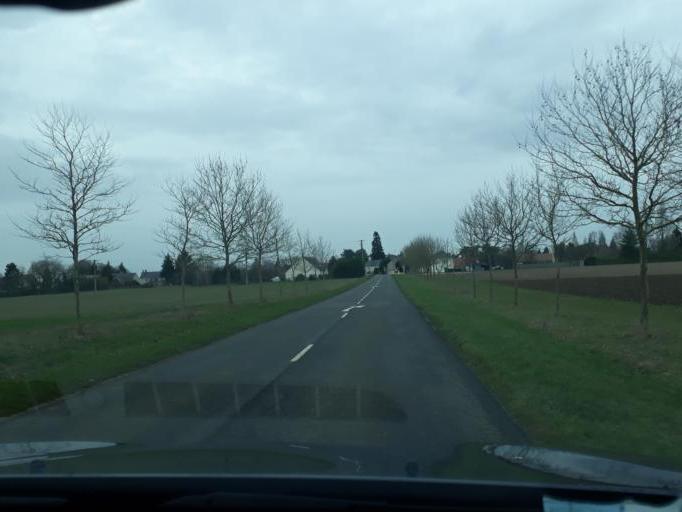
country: FR
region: Centre
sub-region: Departement du Loiret
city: Tavers
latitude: 47.7929
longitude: 1.5327
